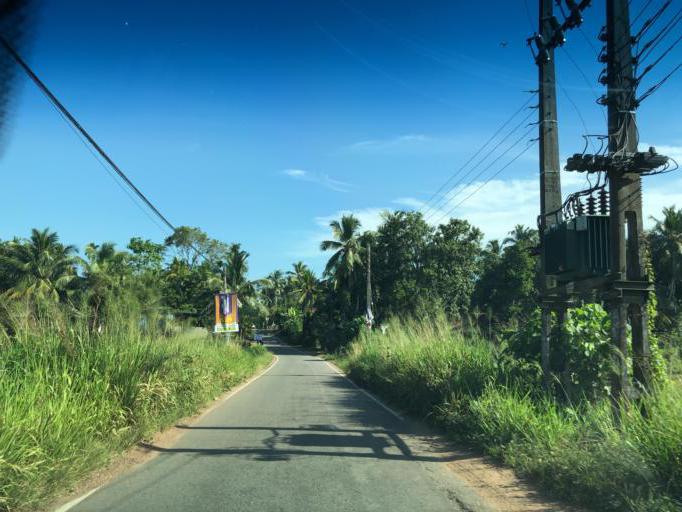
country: LK
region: Western
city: Homagama
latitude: 6.7867
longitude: 79.9786
